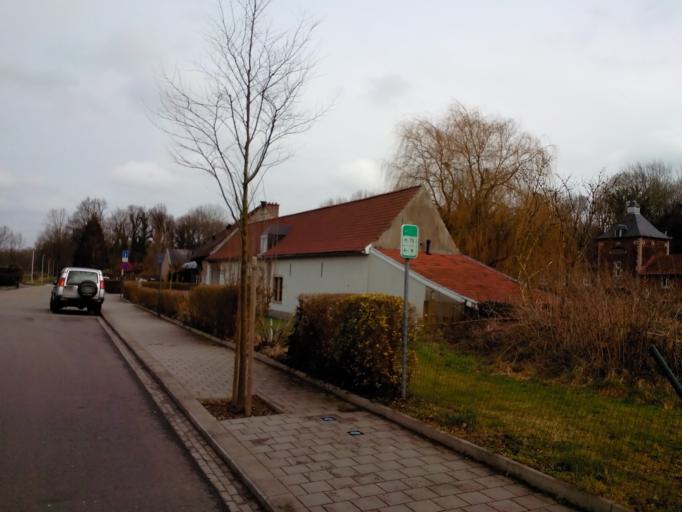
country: BE
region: Flanders
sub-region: Provincie Vlaams-Brabant
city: Oud-Heverlee
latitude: 50.8608
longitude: 4.6641
